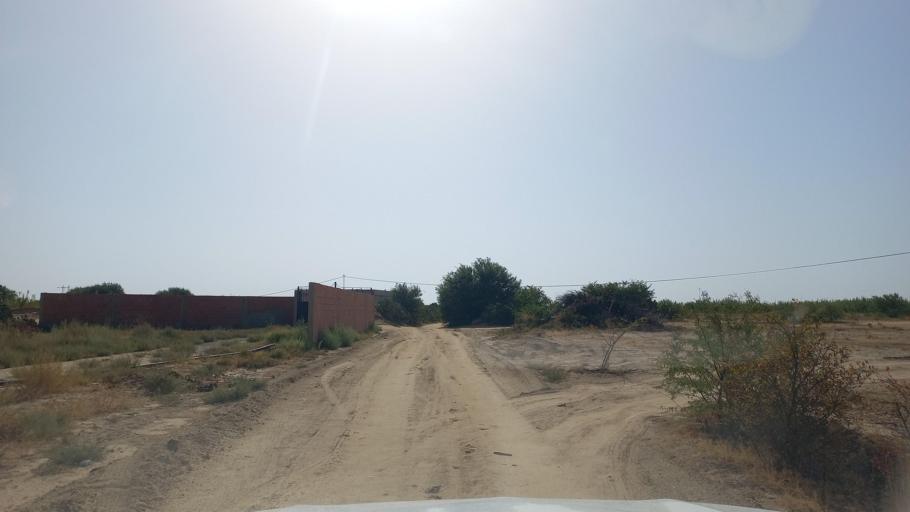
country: TN
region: Al Qasrayn
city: Kasserine
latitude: 35.2454
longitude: 9.0420
